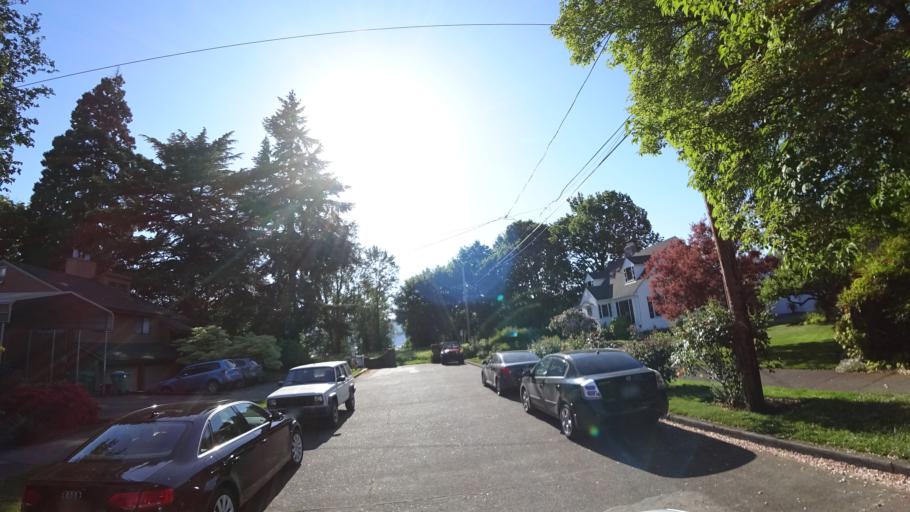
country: US
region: Oregon
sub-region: Multnomah County
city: Portland
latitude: 45.5550
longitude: -122.6906
